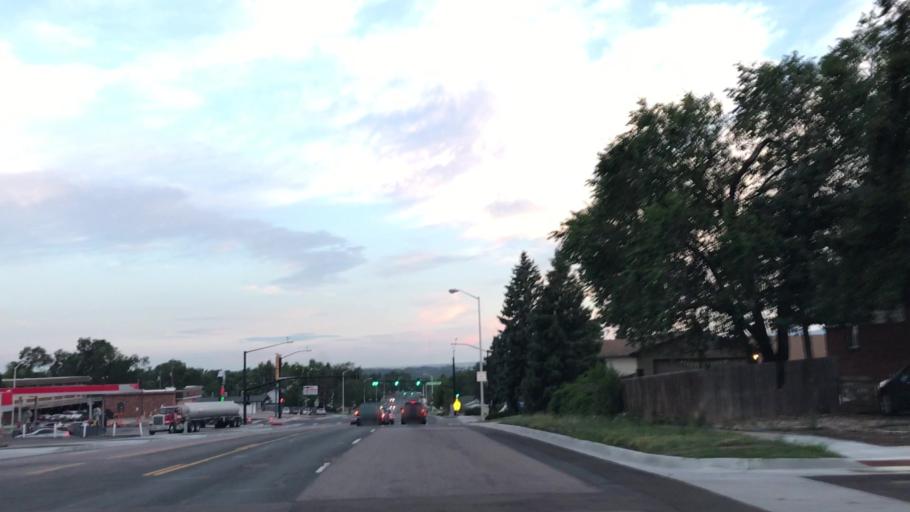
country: US
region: Colorado
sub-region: El Paso County
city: Colorado Springs
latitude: 38.8339
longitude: -104.7760
